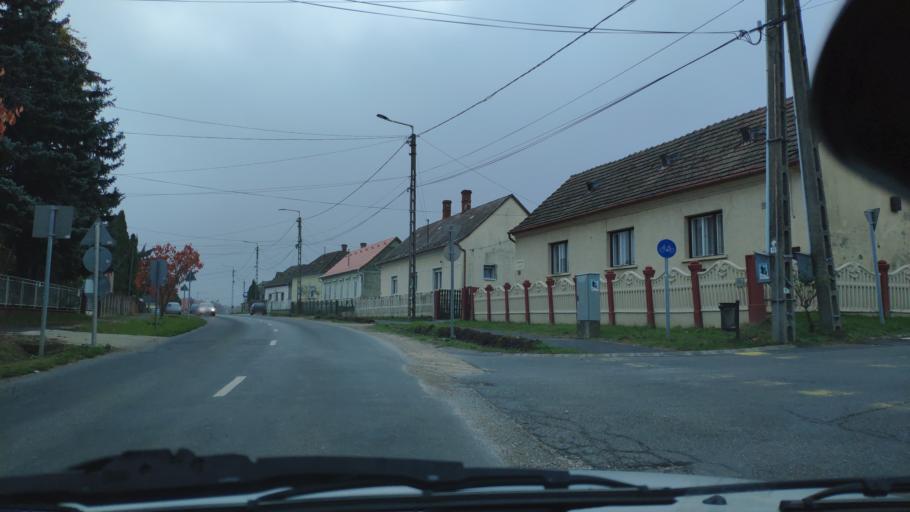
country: HU
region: Zala
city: Zalakomar
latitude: 46.5601
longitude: 17.1227
